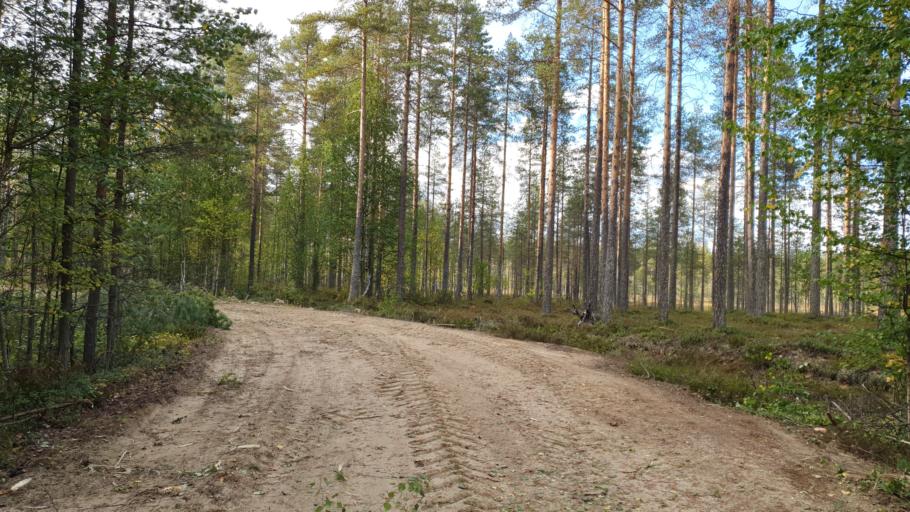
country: FI
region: Kainuu
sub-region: Kehys-Kainuu
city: Kuhmo
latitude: 64.2029
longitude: 29.1671
